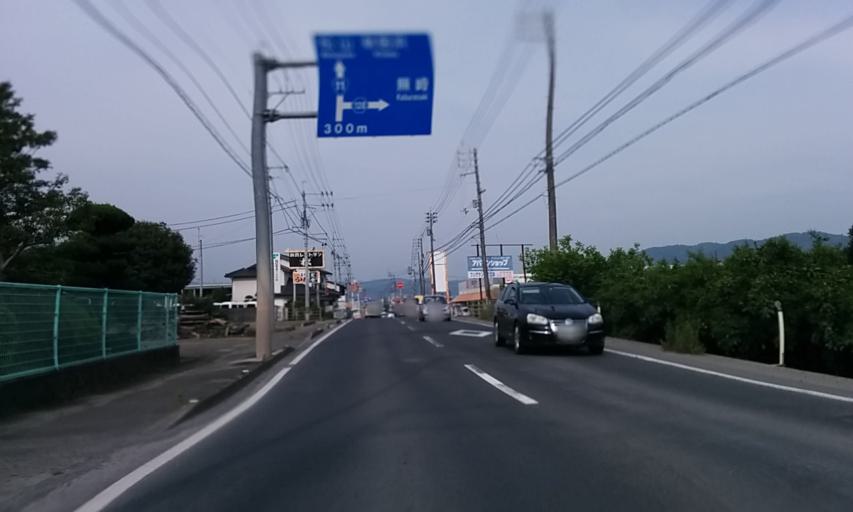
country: JP
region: Ehime
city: Niihama
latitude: 33.9574
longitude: 133.4345
